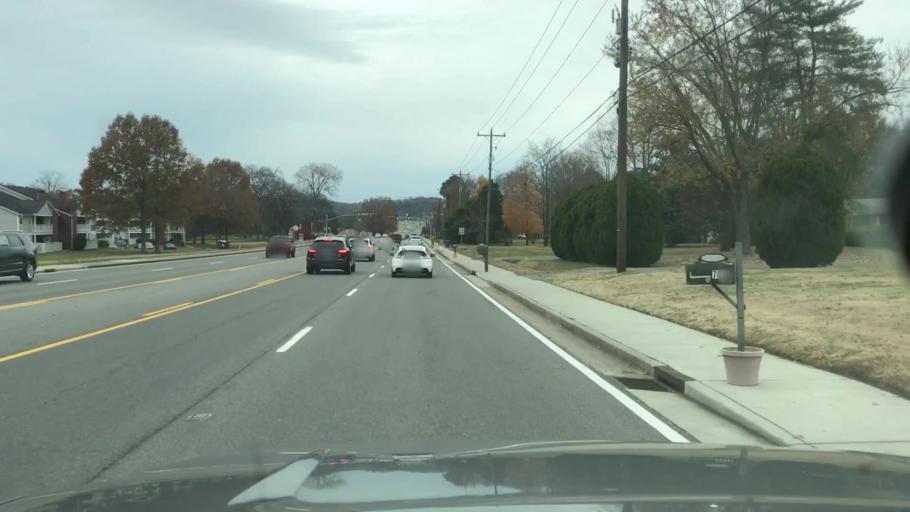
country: US
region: Tennessee
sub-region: Davidson County
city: Belle Meade
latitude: 36.0748
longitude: -86.9379
